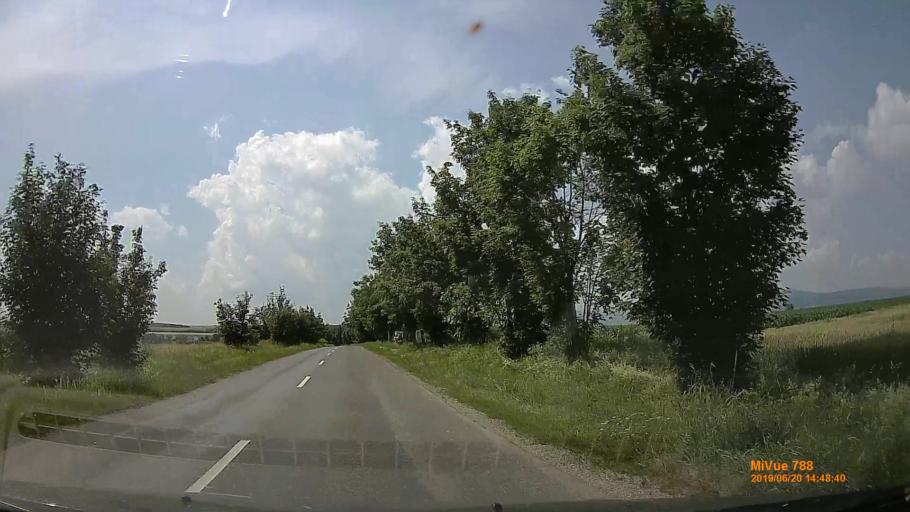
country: HU
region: Baranya
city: Kozarmisleny
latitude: 46.0156
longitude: 18.2851
